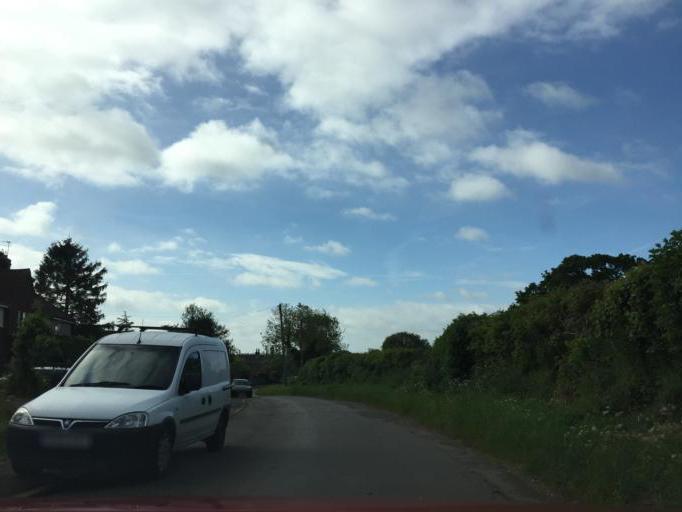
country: GB
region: England
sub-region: Northamptonshire
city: Blisworth
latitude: 52.1437
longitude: -0.9414
